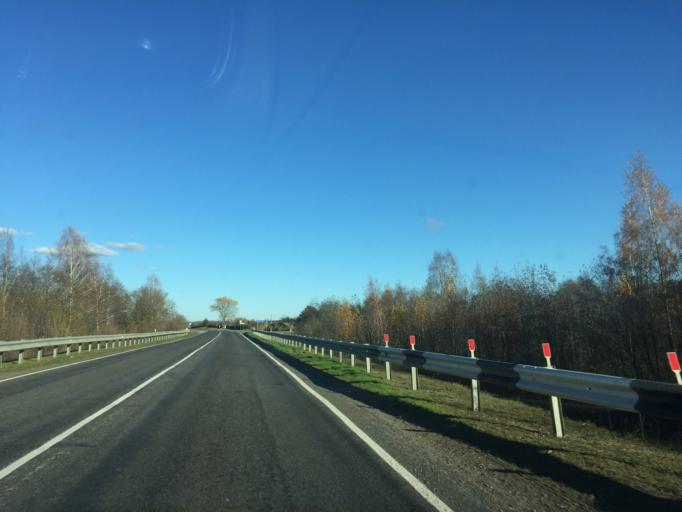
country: BY
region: Vitebsk
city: Dzisna
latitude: 55.2400
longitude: 28.0621
